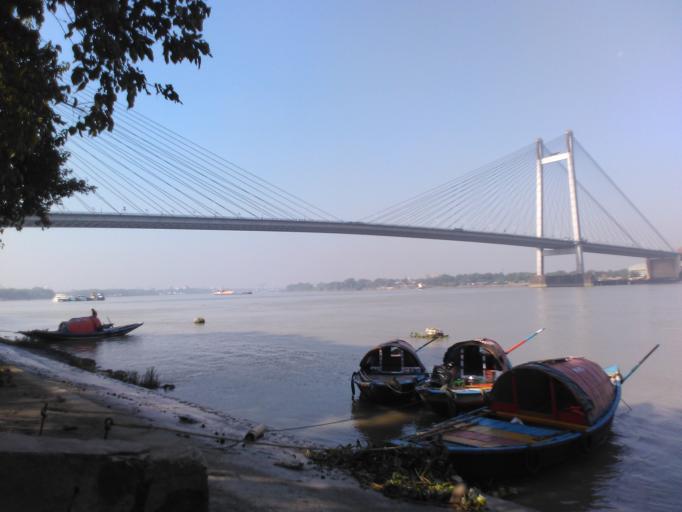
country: IN
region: West Bengal
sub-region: Kolkata
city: Bara Bazar
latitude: 22.5575
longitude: 88.3317
